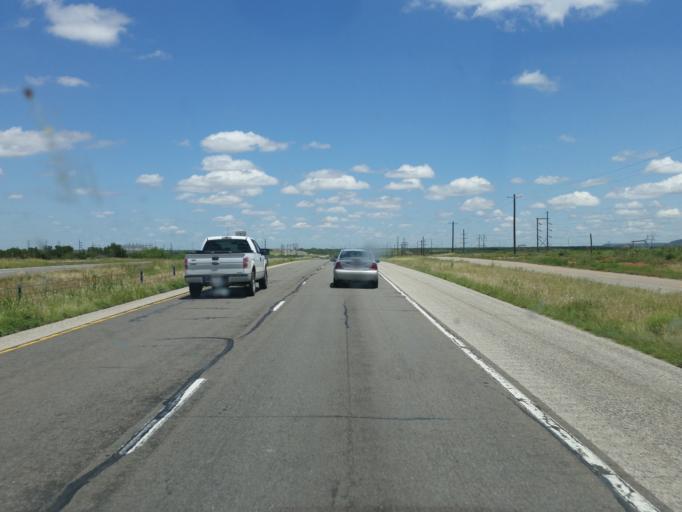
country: US
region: Texas
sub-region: Nolan County
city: Sweetwater
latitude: 32.4916
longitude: -100.2499
